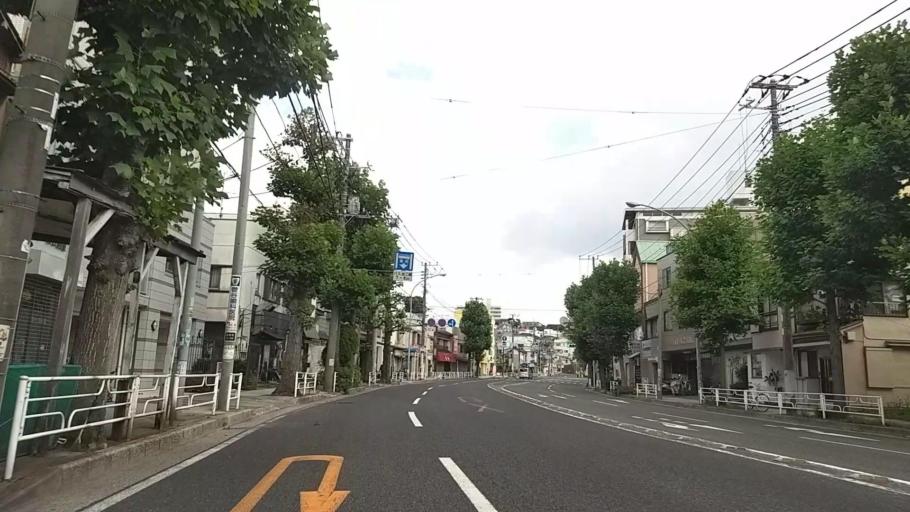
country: JP
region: Kanagawa
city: Yokohama
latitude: 35.4328
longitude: 139.6485
